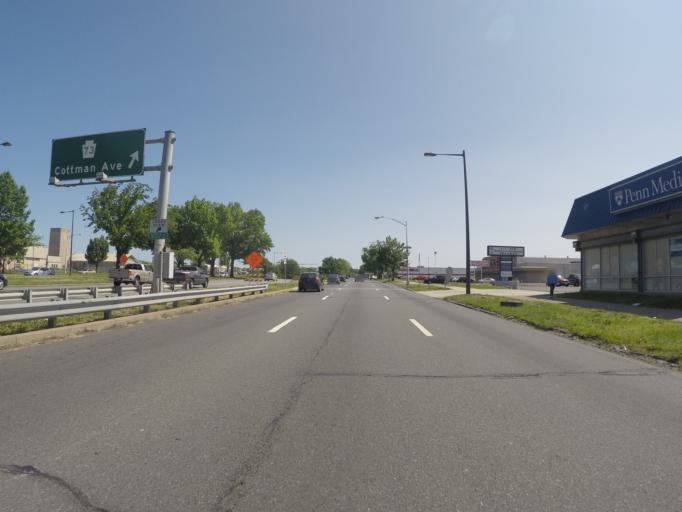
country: US
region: New Jersey
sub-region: Burlington County
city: Palmyra
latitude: 40.0420
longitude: -75.0565
